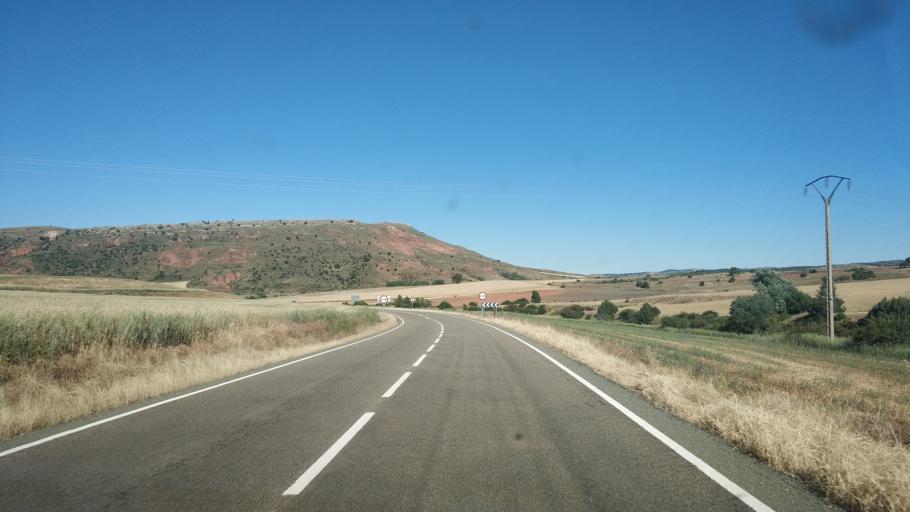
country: ES
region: Castille and Leon
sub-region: Provincia de Soria
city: Montejo de Tiermes
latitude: 41.3468
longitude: -3.1531
